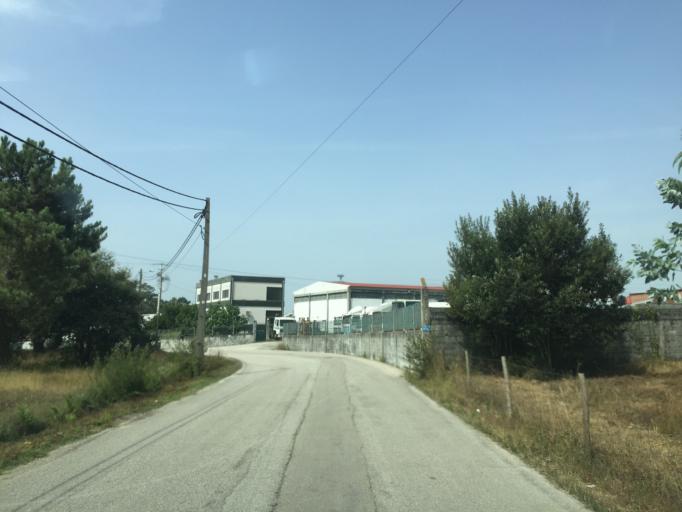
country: PT
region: Leiria
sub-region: Leiria
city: Amor
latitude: 39.7957
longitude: -8.8308
